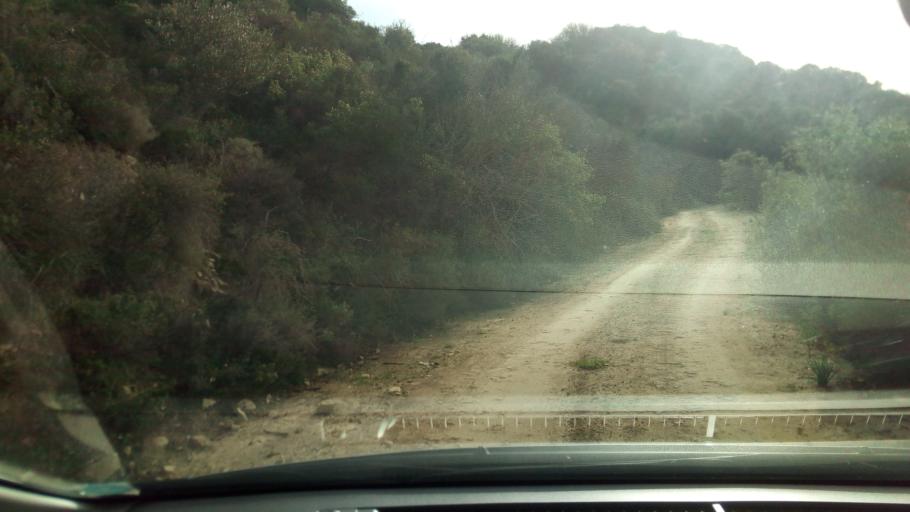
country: CY
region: Pafos
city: Mesogi
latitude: 34.7985
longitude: 32.5471
